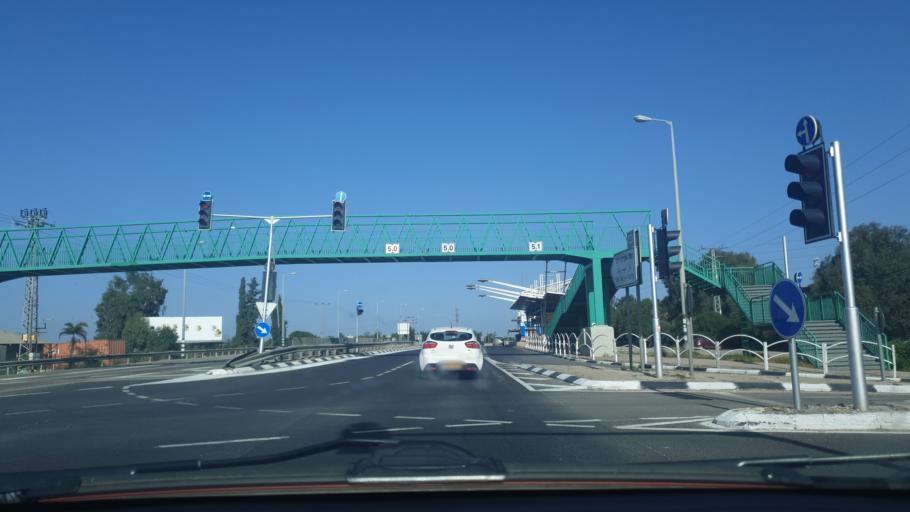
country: IL
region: Central District
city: Kefar Habad
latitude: 31.9692
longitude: 34.8439
